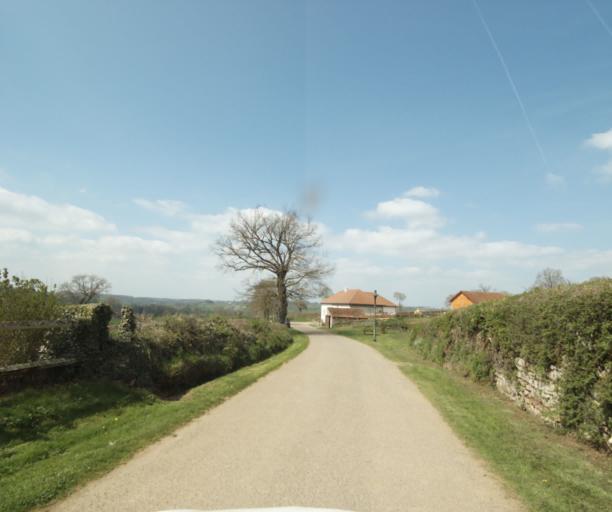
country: FR
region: Bourgogne
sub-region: Departement de Saone-et-Loire
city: Charolles
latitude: 46.4011
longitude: 4.3001
